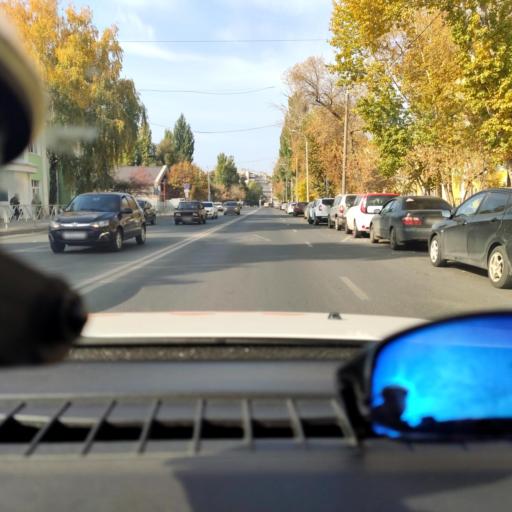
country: RU
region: Samara
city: Samara
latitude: 53.1905
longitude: 50.1292
